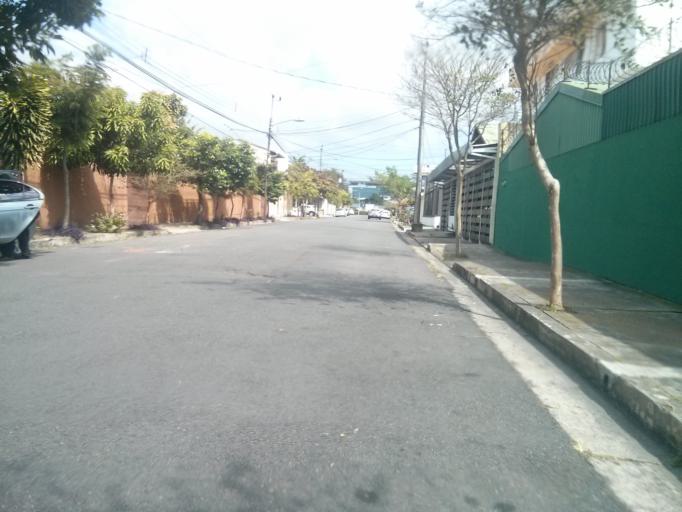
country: CR
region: San Jose
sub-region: Canton de Goicoechea
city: Guadalupe
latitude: 9.9352
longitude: -84.0643
